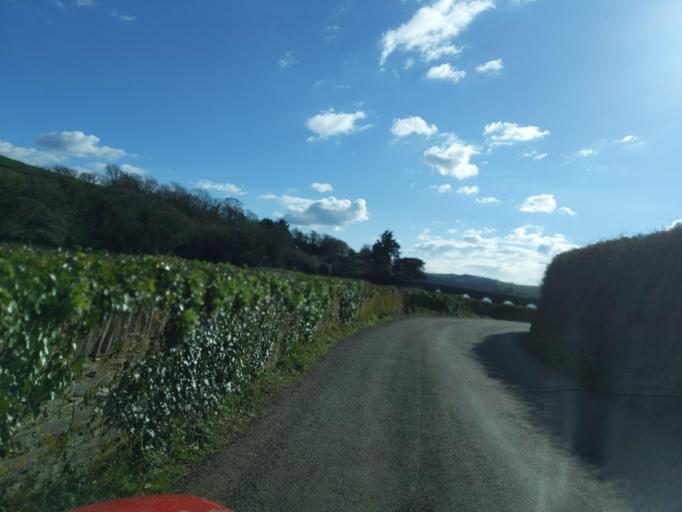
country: GB
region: England
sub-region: Devon
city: Kingsbridge
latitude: 50.2770
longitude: -3.7612
